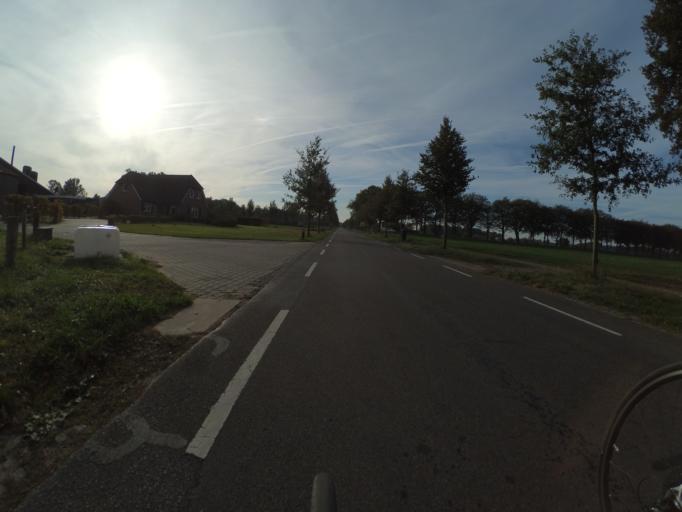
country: NL
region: Overijssel
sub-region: Gemeente Deventer
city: Schalkhaar
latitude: 52.2870
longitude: 6.2726
